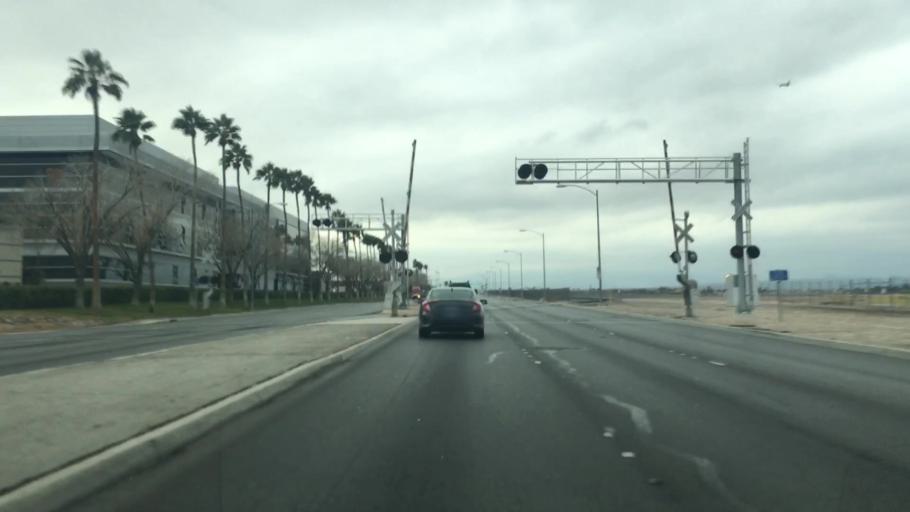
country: US
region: Nevada
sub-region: Clark County
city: Paradise
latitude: 36.0714
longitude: -115.1577
